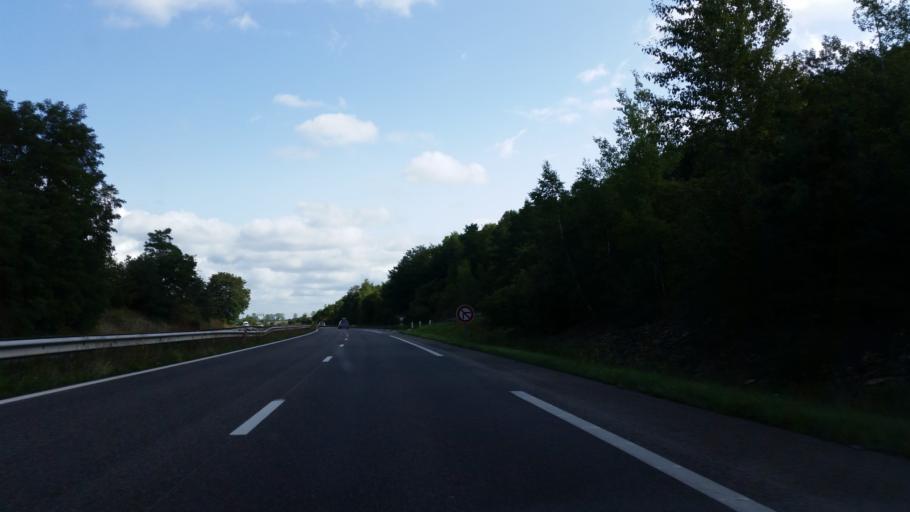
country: FR
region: Lorraine
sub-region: Departement de Meurthe-et-Moselle
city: Bayon
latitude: 48.4622
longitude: 6.2447
